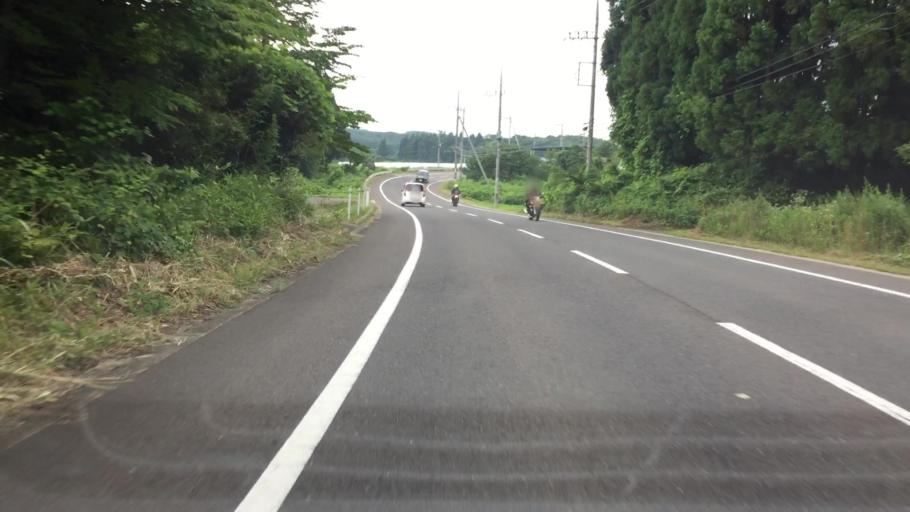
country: JP
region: Tochigi
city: Kuroiso
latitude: 37.0749
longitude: 140.0484
